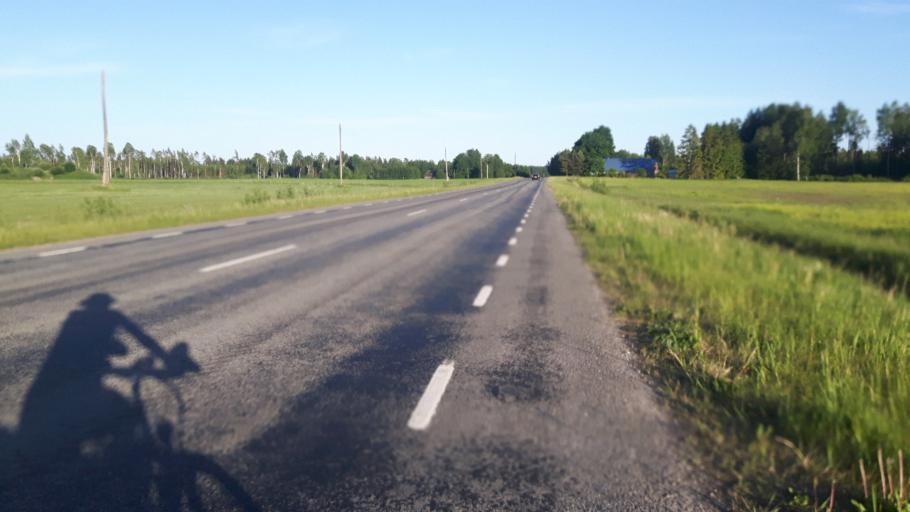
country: EE
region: Raplamaa
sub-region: Jaervakandi vald
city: Jarvakandi
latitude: 58.7860
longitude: 24.9364
